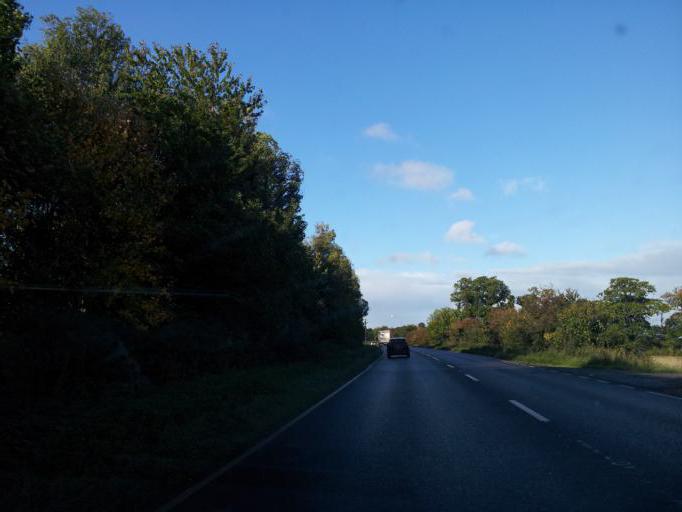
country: GB
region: England
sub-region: Norfolk
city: King's Lynn
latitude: 52.7162
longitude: 0.4715
